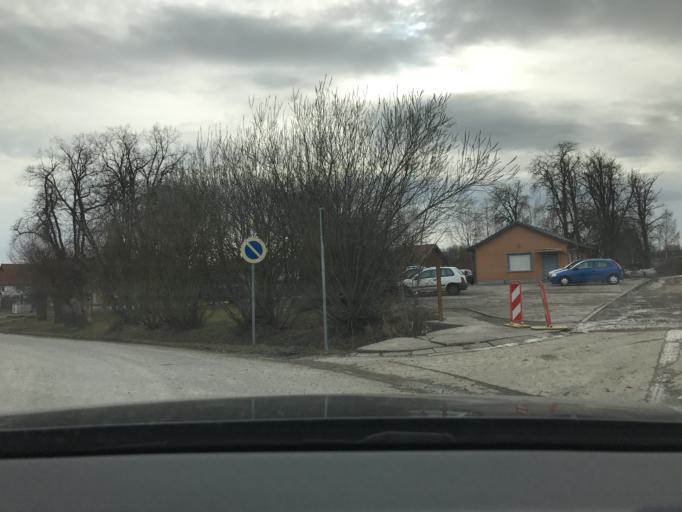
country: DE
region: Thuringia
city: Anrode
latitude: 51.2565
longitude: 10.3906
